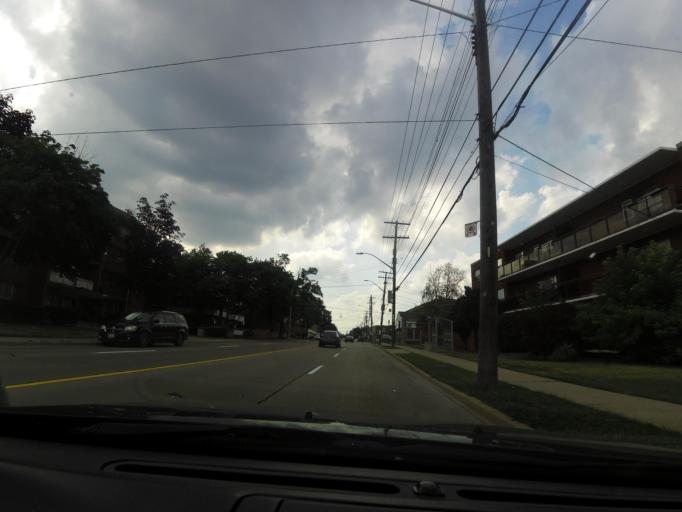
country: CA
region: Ontario
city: Hamilton
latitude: 43.2304
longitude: -79.7992
